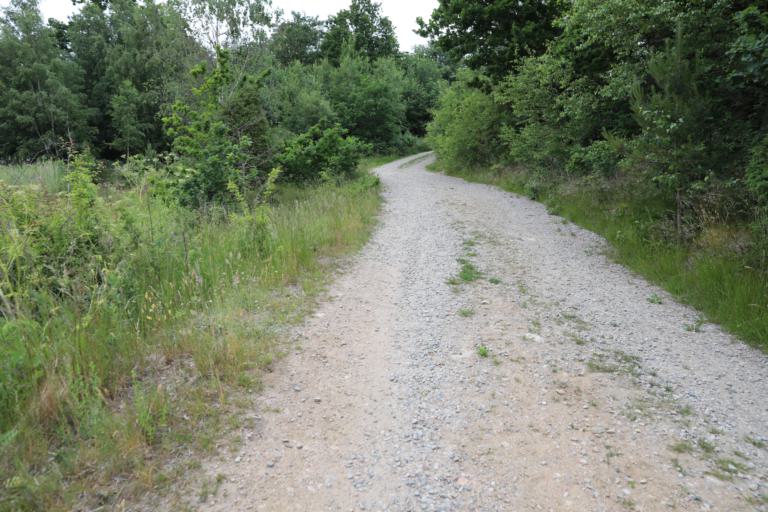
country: SE
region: Halland
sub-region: Varbergs Kommun
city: Varberg
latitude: 57.1656
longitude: 12.2621
